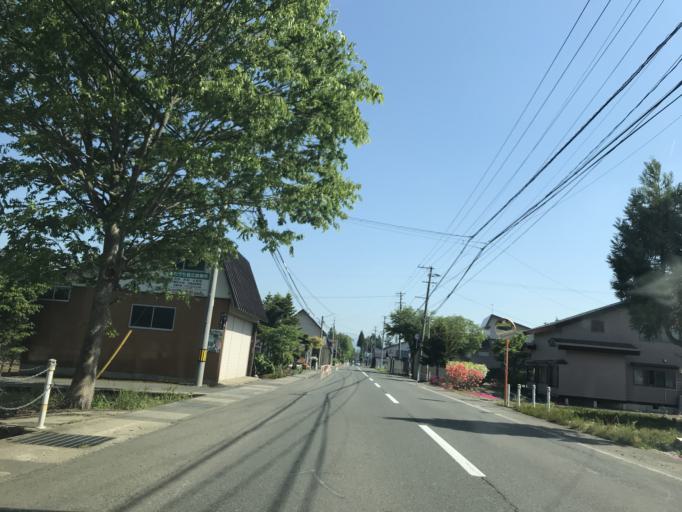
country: JP
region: Akita
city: Yokotemachi
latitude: 39.3987
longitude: 140.7566
